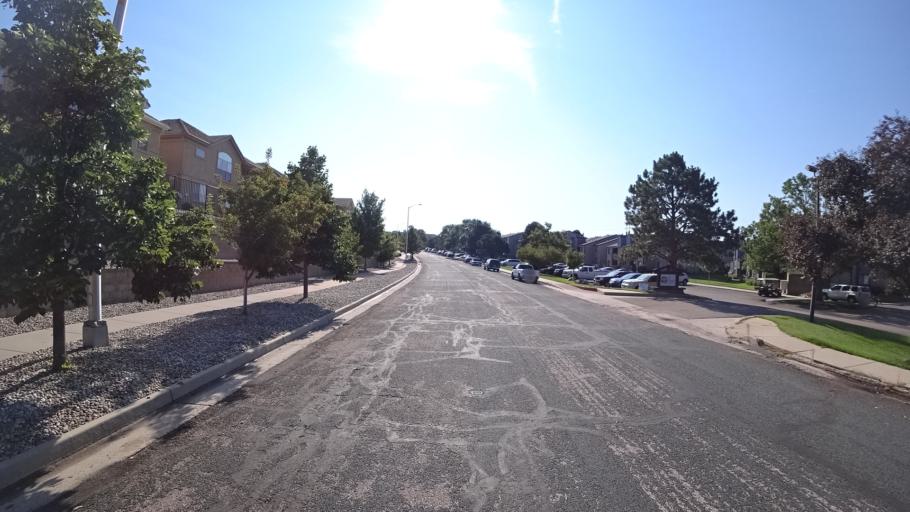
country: US
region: Colorado
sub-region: El Paso County
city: Air Force Academy
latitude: 38.9507
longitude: -104.7868
